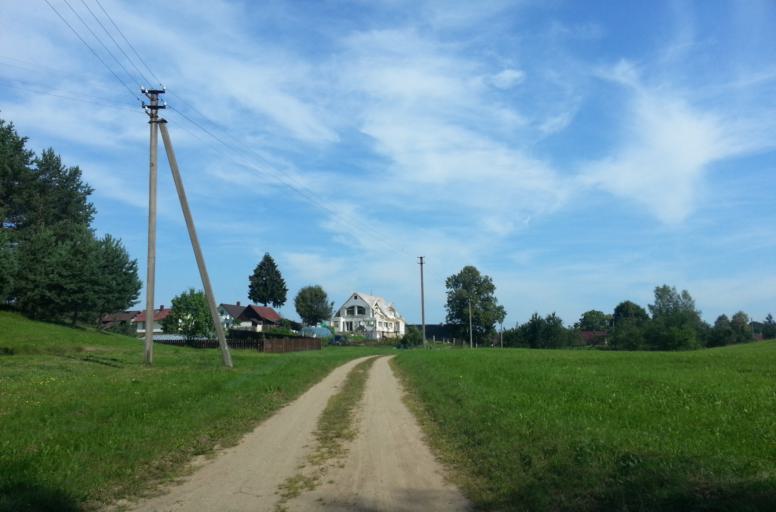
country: LT
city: Grigiskes
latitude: 54.7479
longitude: 25.0229
